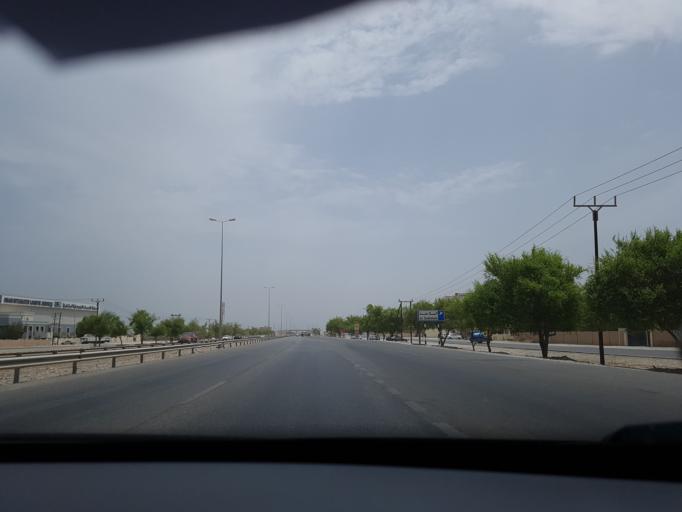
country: OM
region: Al Batinah
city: Barka'
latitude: 23.6600
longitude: 57.9376
